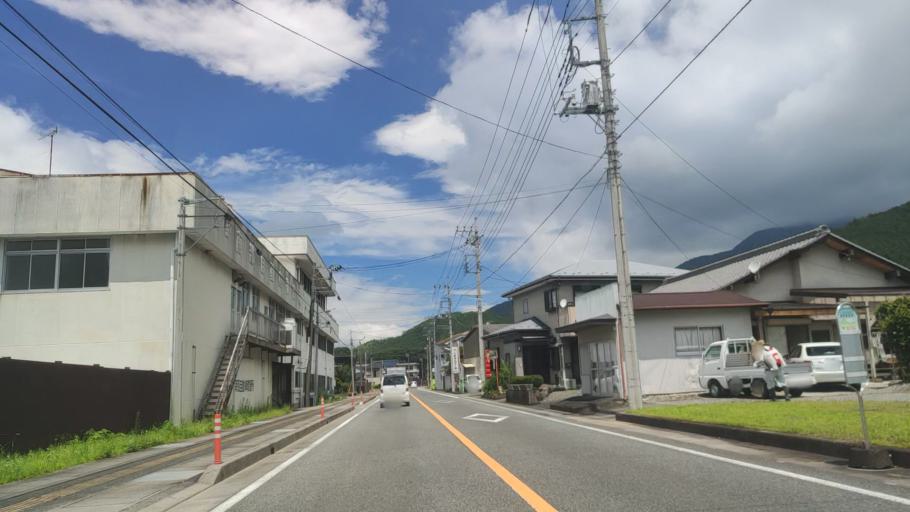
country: JP
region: Shizuoka
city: Fujinomiya
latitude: 35.2773
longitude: 138.4671
